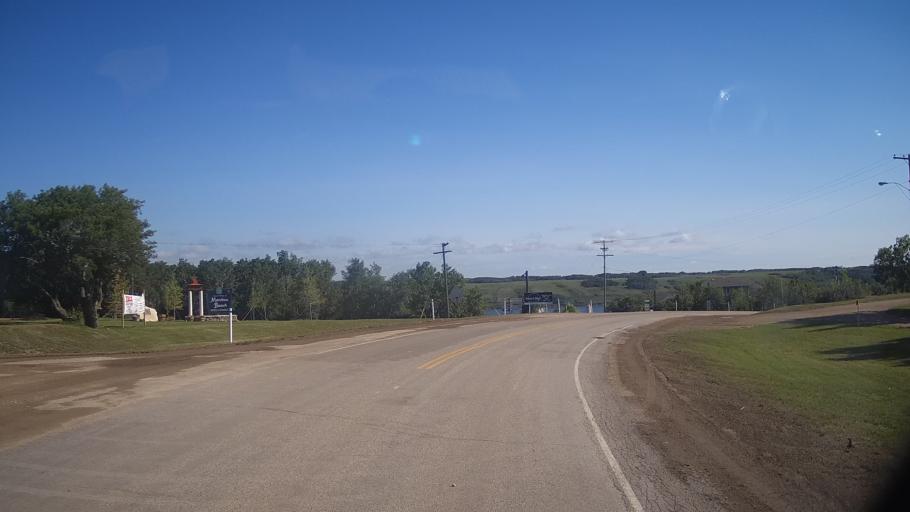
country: CA
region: Saskatchewan
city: Watrous
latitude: 51.7188
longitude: -105.4522
